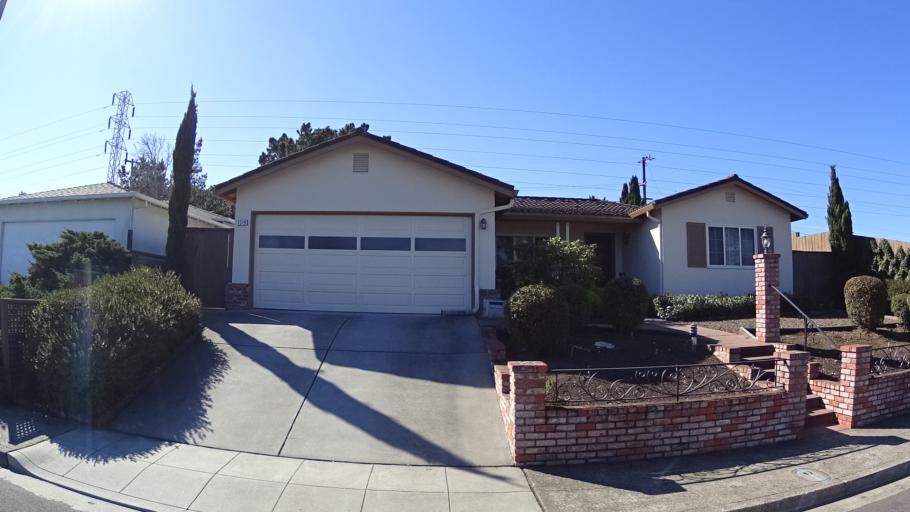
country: US
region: California
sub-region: San Mateo County
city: Hillsborough
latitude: 37.5691
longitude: -122.3935
